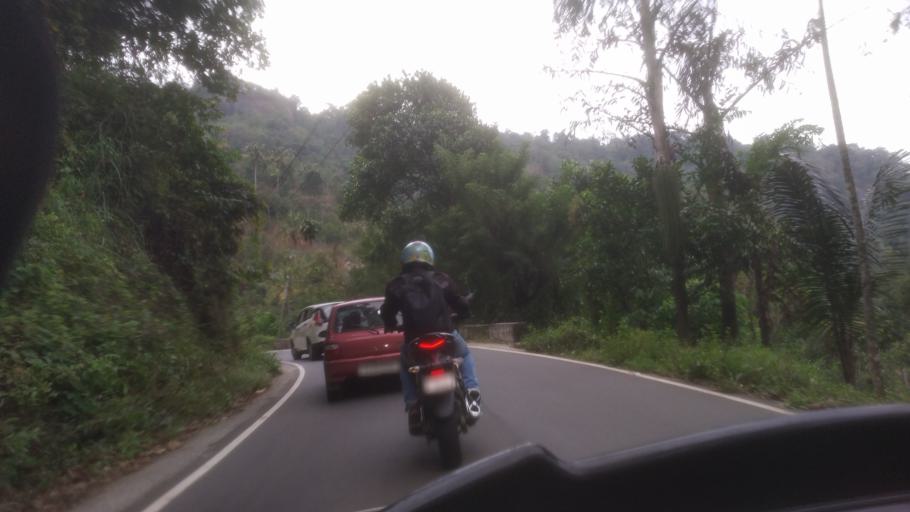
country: IN
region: Kerala
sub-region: Idukki
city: Idukki
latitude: 9.9604
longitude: 77.0078
